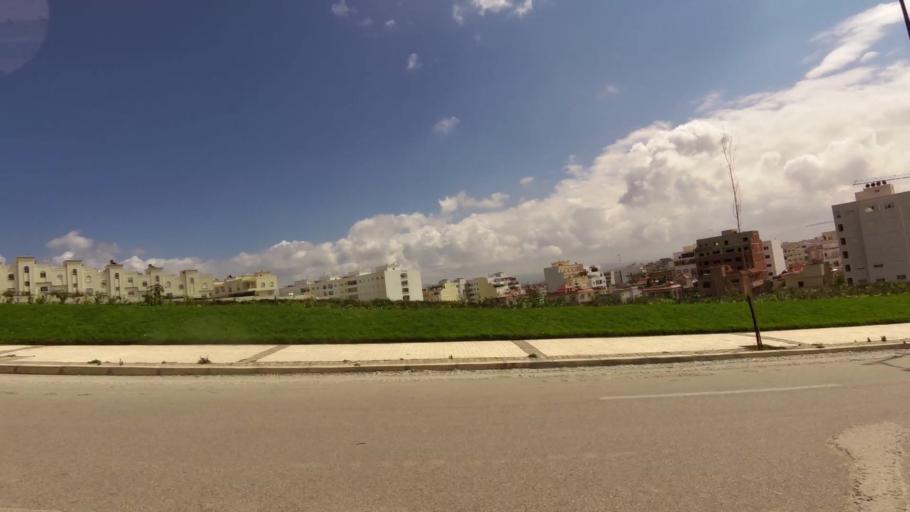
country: MA
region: Tanger-Tetouan
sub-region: Tanger-Assilah
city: Tangier
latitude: 35.7666
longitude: -5.8394
